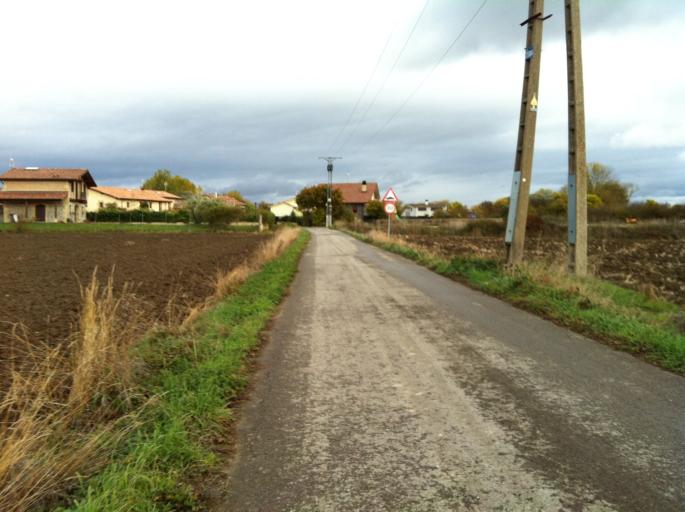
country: ES
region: Basque Country
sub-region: Provincia de Alava
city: Gasteiz / Vitoria
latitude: 42.8758
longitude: -2.7030
